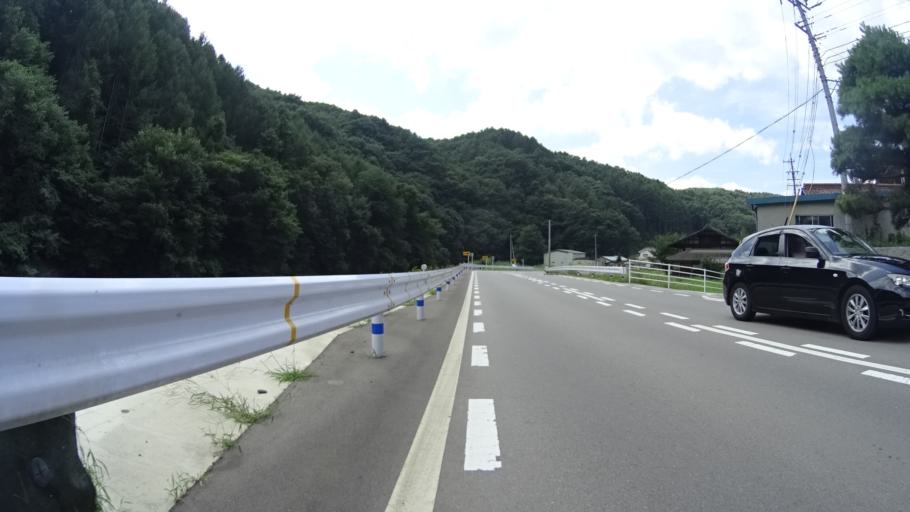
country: JP
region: Nagano
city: Saku
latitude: 36.0664
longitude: 138.5023
